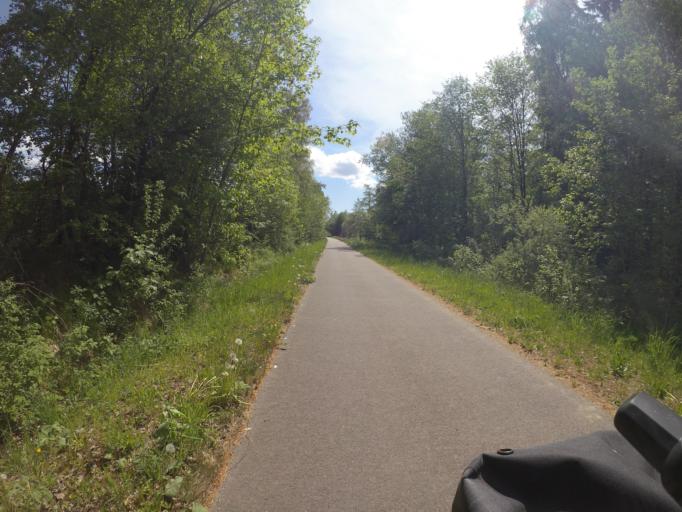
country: BE
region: Wallonia
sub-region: Province de Liege
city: Bullange
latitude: 50.3764
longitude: 6.3156
